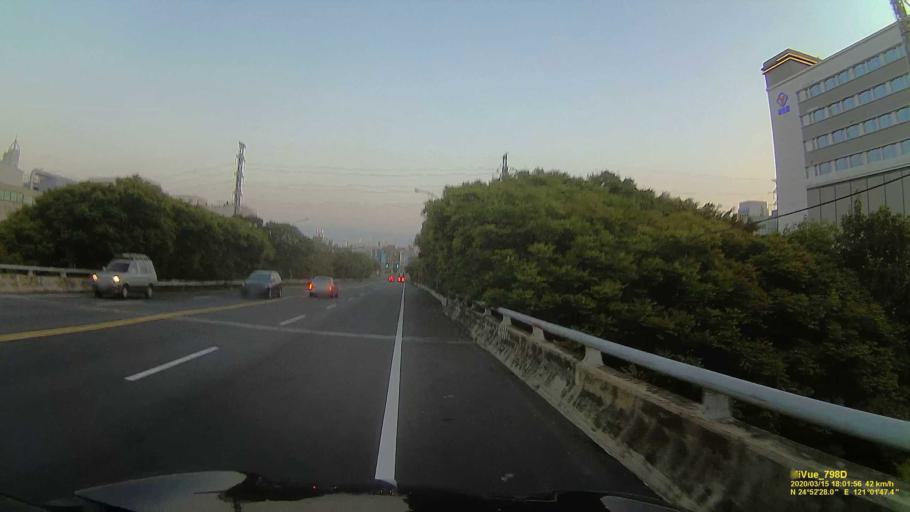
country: TW
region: Taiwan
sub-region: Hsinchu
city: Zhubei
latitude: 24.8743
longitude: 121.0299
